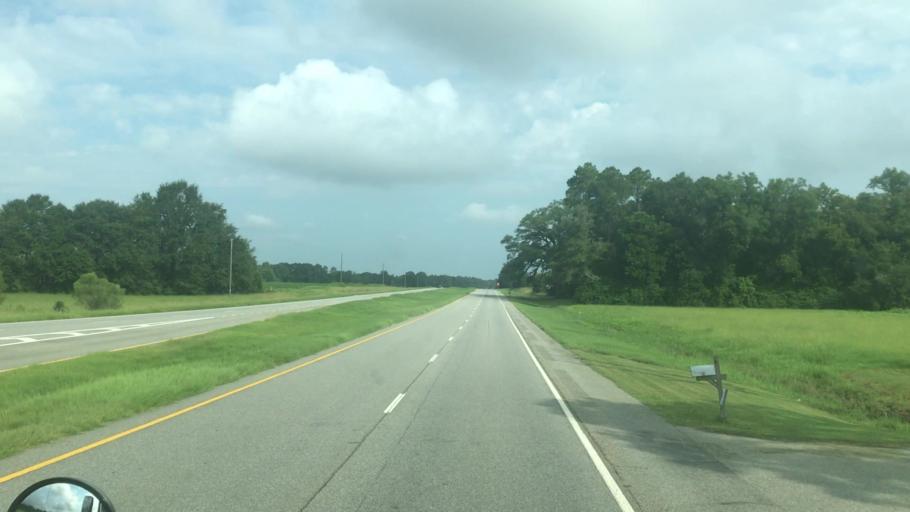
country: US
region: Georgia
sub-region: Miller County
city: Colquitt
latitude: 31.2663
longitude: -84.8199
